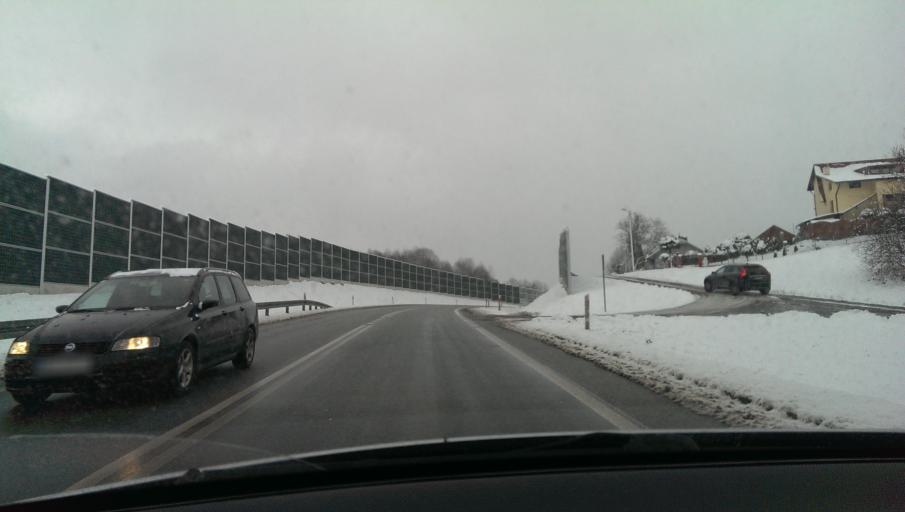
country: PL
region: Subcarpathian Voivodeship
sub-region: Powiat brzozowski
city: Brzozow
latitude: 49.6889
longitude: 22.0352
